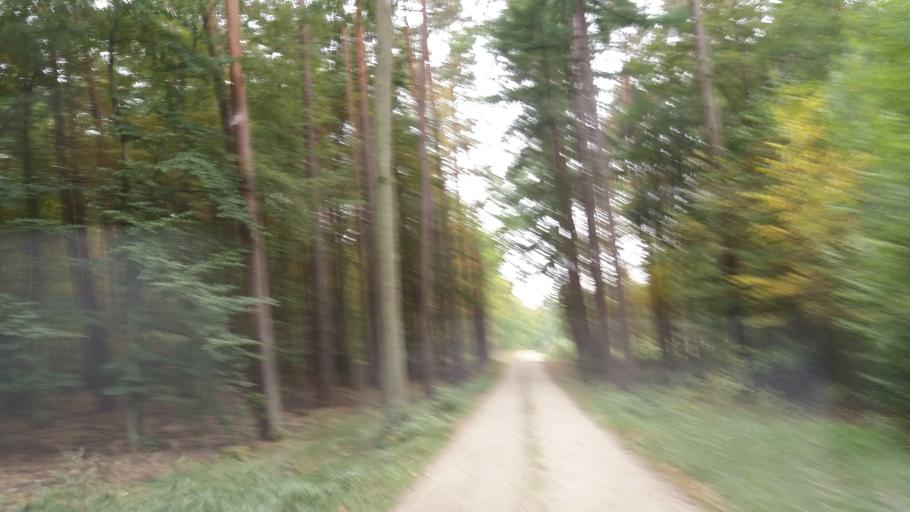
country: PL
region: West Pomeranian Voivodeship
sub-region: Powiat mysliborski
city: Barlinek
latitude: 52.9191
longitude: 15.2127
